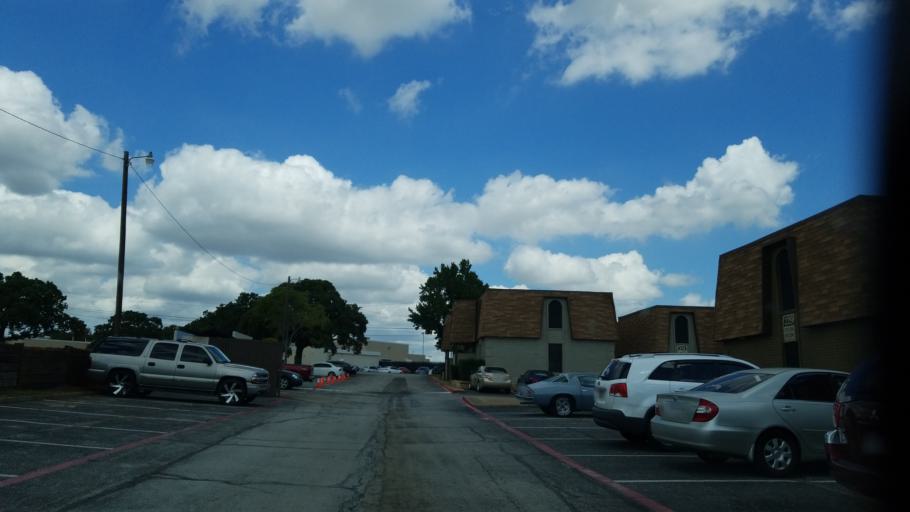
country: US
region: Texas
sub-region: Tarrant County
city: Euless
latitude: 32.8403
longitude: -97.0966
